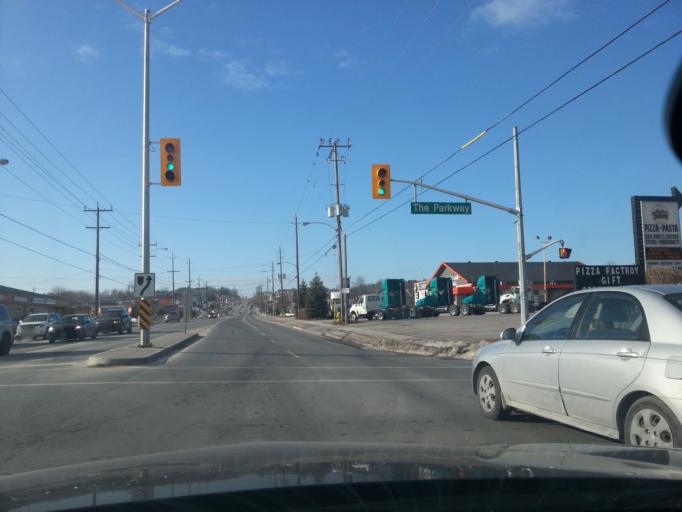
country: CA
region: Ontario
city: Peterborough
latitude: 44.2823
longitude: -78.3439
